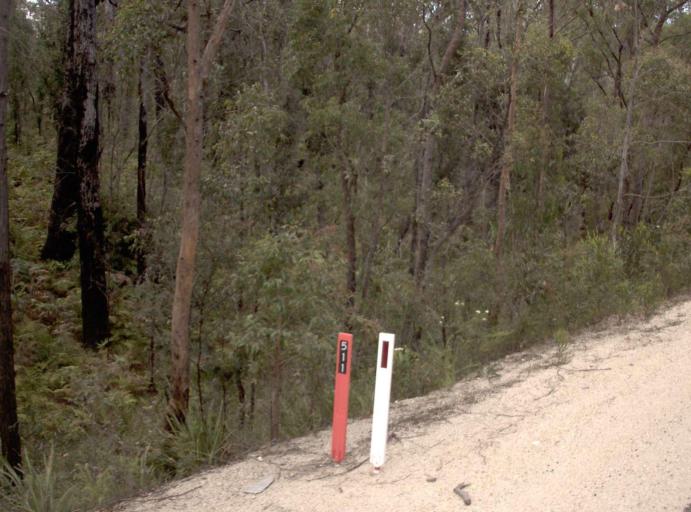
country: AU
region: New South Wales
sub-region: Bega Valley
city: Eden
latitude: -37.4016
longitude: 149.6689
